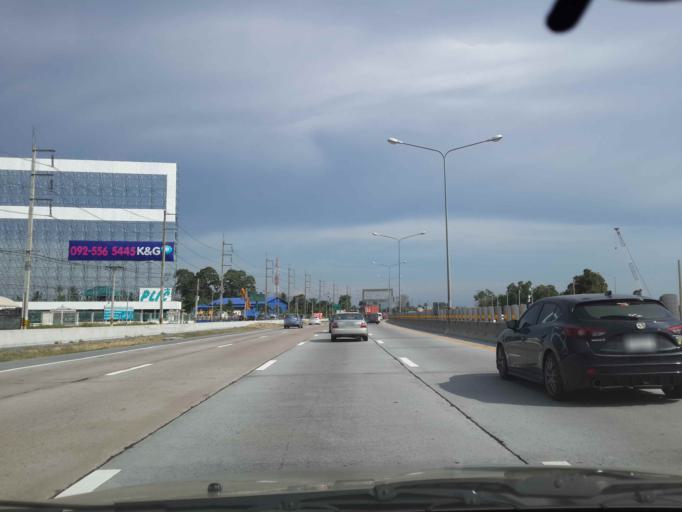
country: TH
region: Chon Buri
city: Si Racha
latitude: 13.2165
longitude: 101.0056
